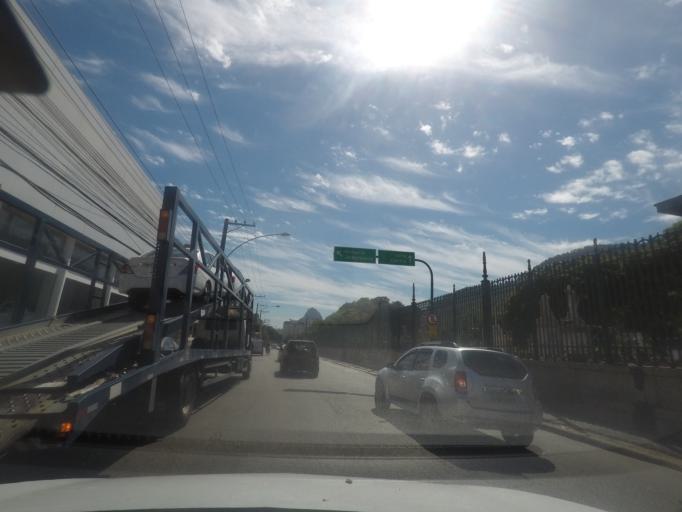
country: BR
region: Rio de Janeiro
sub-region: Rio De Janeiro
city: Rio de Janeiro
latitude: -22.9581
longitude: -43.1908
